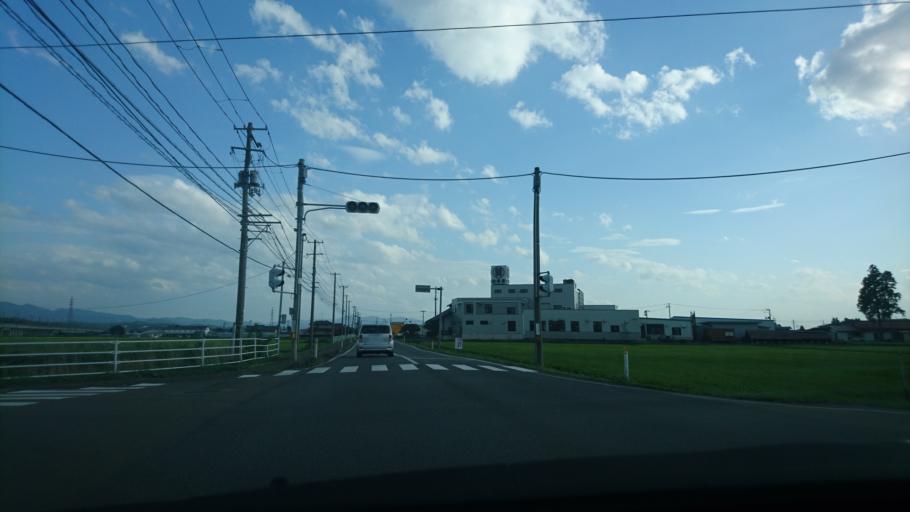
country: JP
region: Iwate
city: Mizusawa
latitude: 39.1644
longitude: 141.1804
